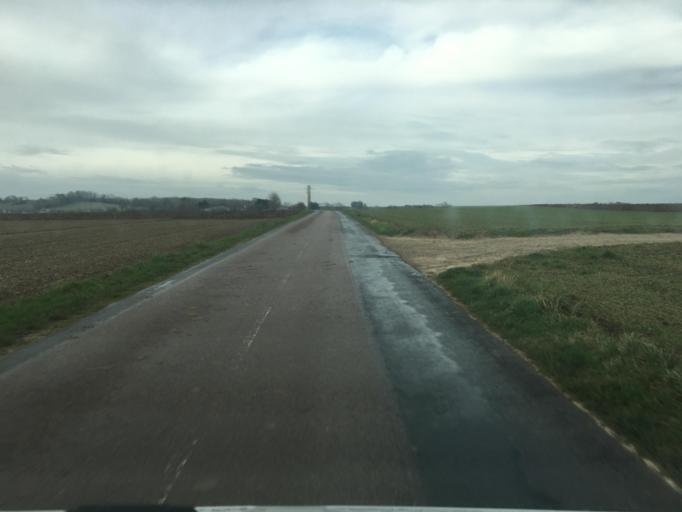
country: FR
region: Lower Normandy
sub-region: Departement du Calvados
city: Ver-sur-Mer
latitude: 49.3296
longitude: -0.5910
